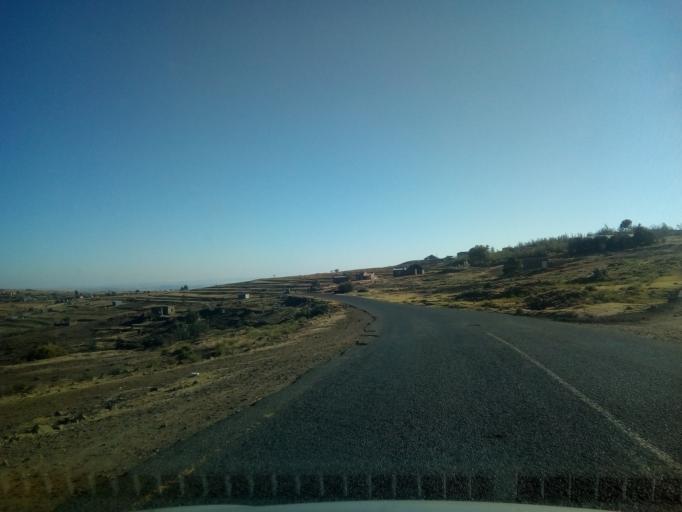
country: LS
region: Berea
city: Teyateyaneng
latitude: -29.2591
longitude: 27.8042
